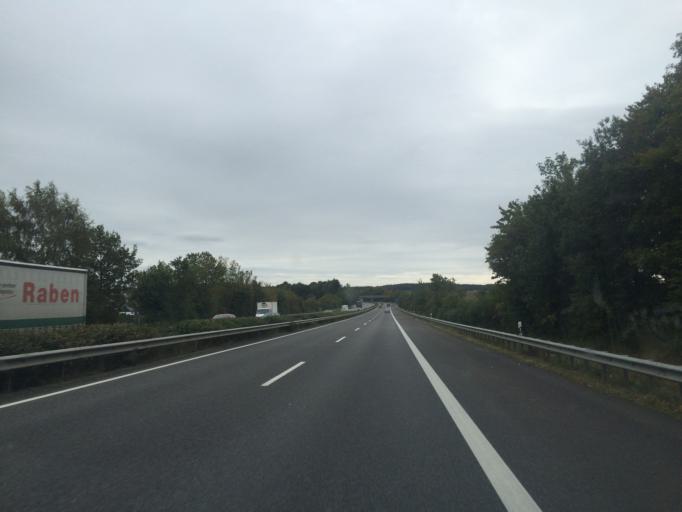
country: DE
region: Rheinland-Pfalz
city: Hasborn
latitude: 50.0581
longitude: 6.9020
